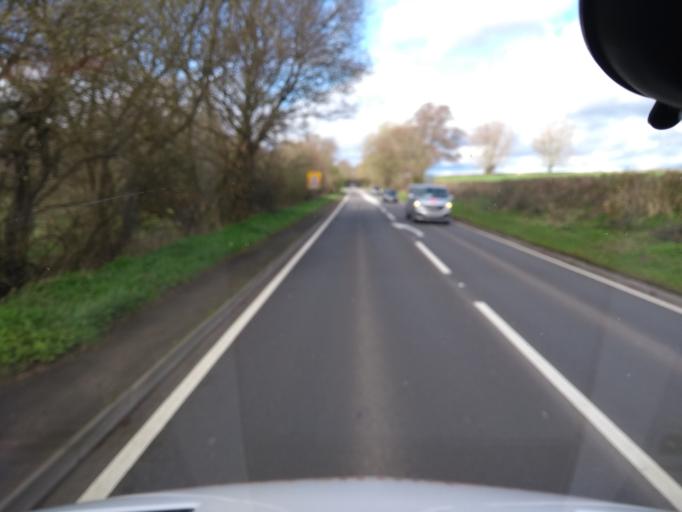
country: GB
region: England
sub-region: Somerset
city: Stoke-sub-Hamdon
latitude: 50.9575
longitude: -2.7183
